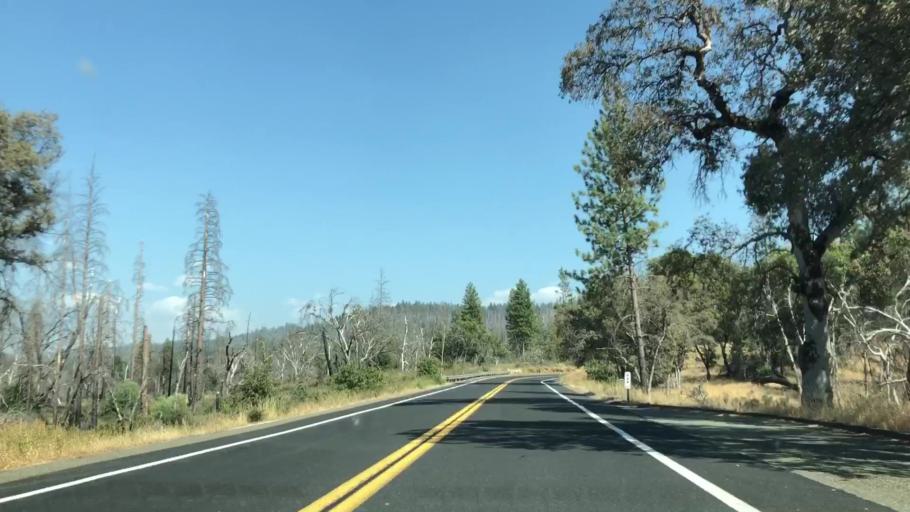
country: US
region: California
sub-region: Tuolumne County
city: Tuolumne City
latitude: 37.8246
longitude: -120.0078
